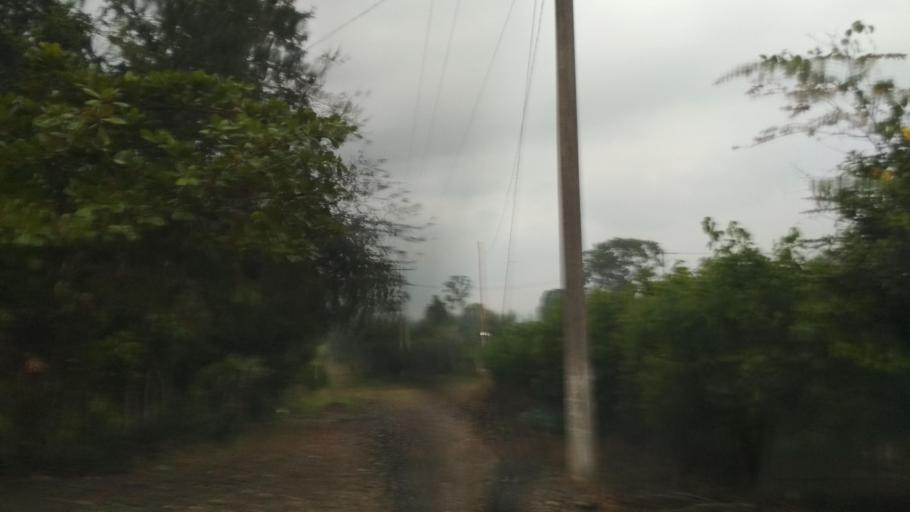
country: MM
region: Shan
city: Taunggyi
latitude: 20.3059
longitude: 97.3030
